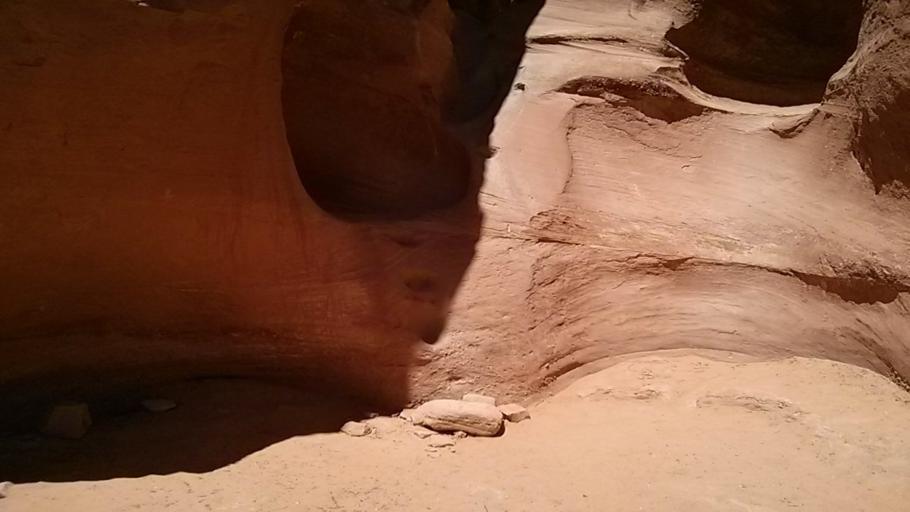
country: US
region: Arizona
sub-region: Coconino County
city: Page
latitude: 37.4817
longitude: -111.2166
